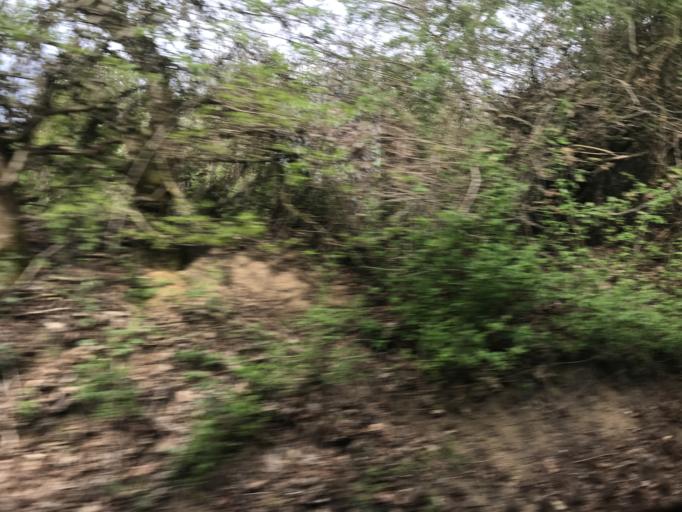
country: DE
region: Hesse
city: Kelkheim (Taunus)
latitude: 50.1506
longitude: 8.4479
